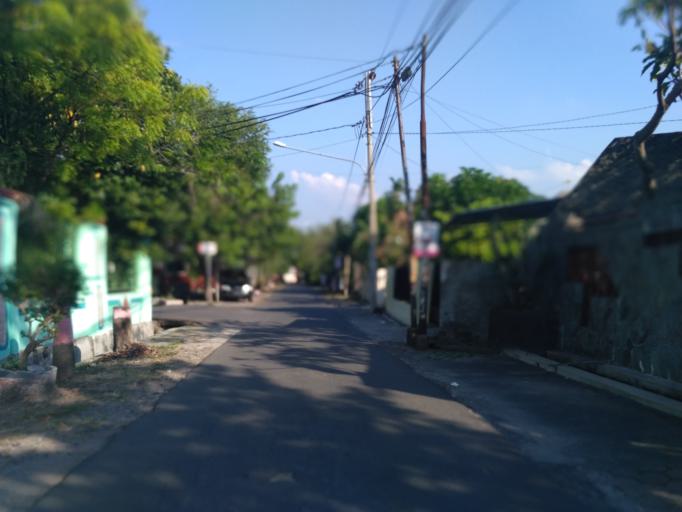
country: ID
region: Central Java
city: Semarang
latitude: -6.9953
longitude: 110.4502
